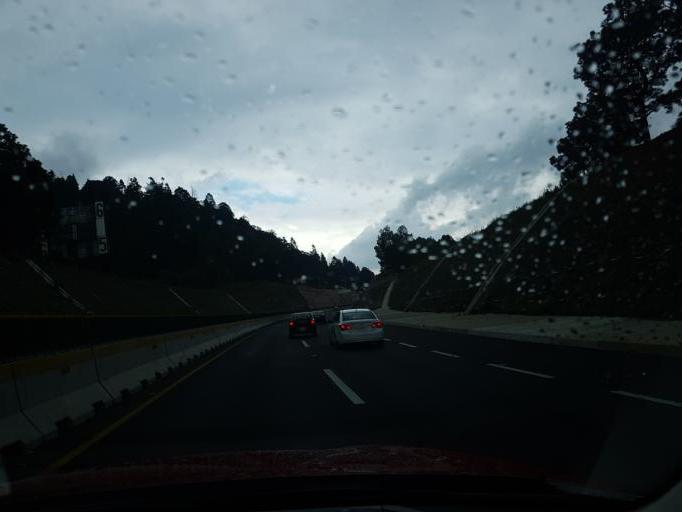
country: MX
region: Morelos
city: San Jeronimo Acazulco
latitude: 19.2984
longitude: -99.4021
